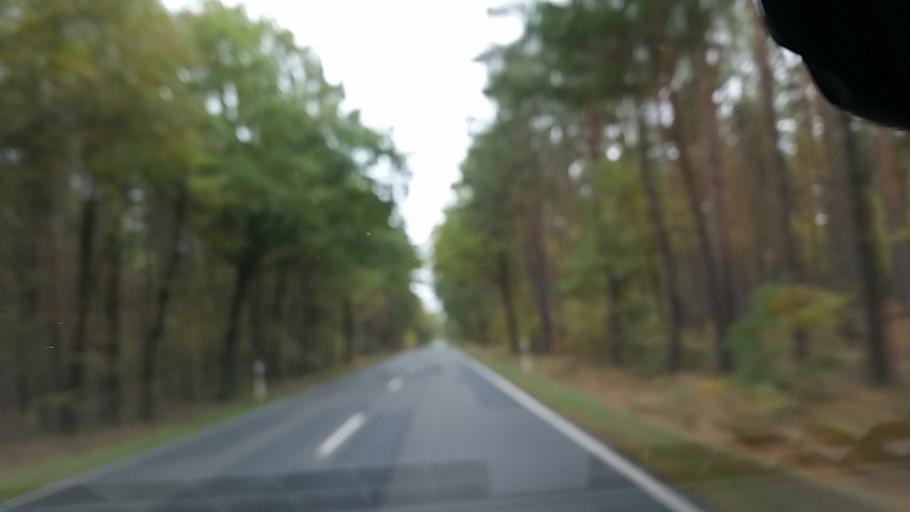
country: DE
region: Lower Saxony
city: Tulau
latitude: 52.6358
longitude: 10.8105
